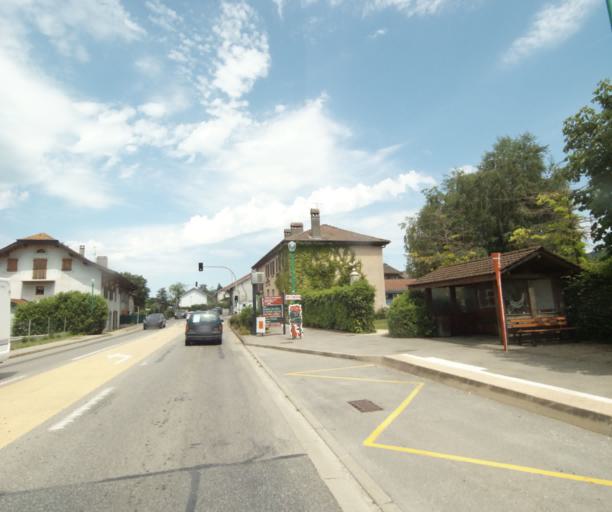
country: FR
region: Rhone-Alpes
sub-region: Departement de la Haute-Savoie
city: Massongy
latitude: 46.3181
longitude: 6.3301
